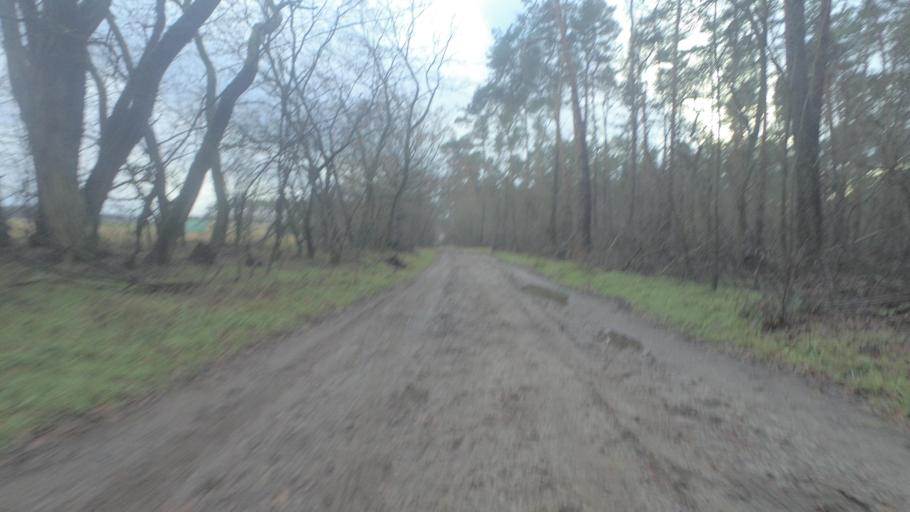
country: DE
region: Brandenburg
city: Ludwigsfelde
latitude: 52.2642
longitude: 13.2380
